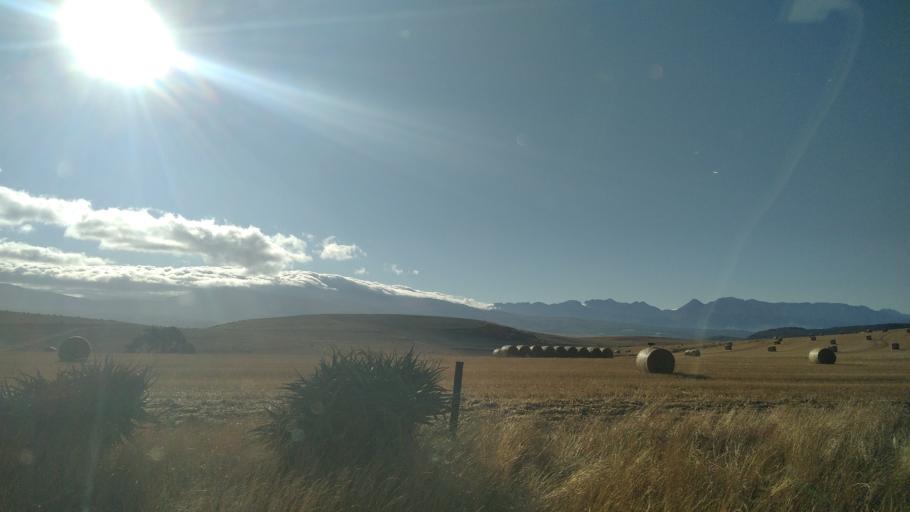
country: ZA
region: Western Cape
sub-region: Overberg District Municipality
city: Caledon
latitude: -34.1401
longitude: 19.2963
